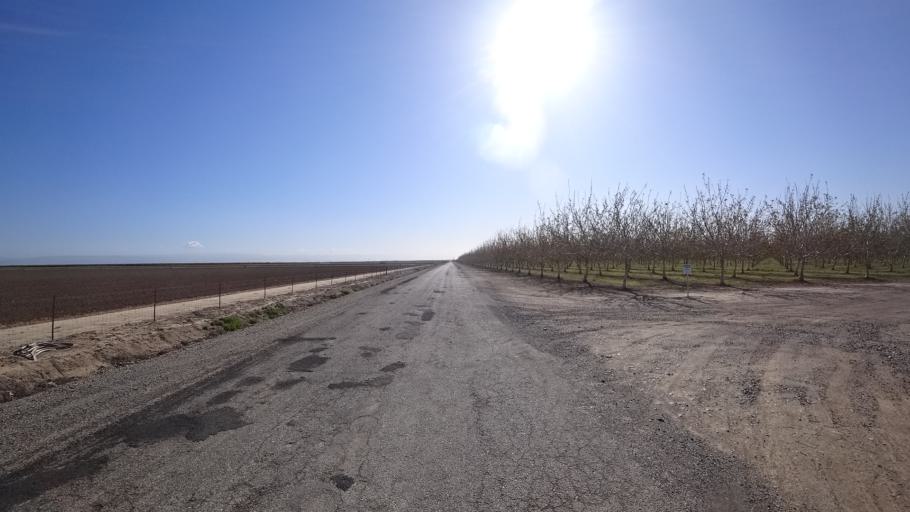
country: US
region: California
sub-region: Glenn County
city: Hamilton City
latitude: 39.6782
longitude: -122.0520
